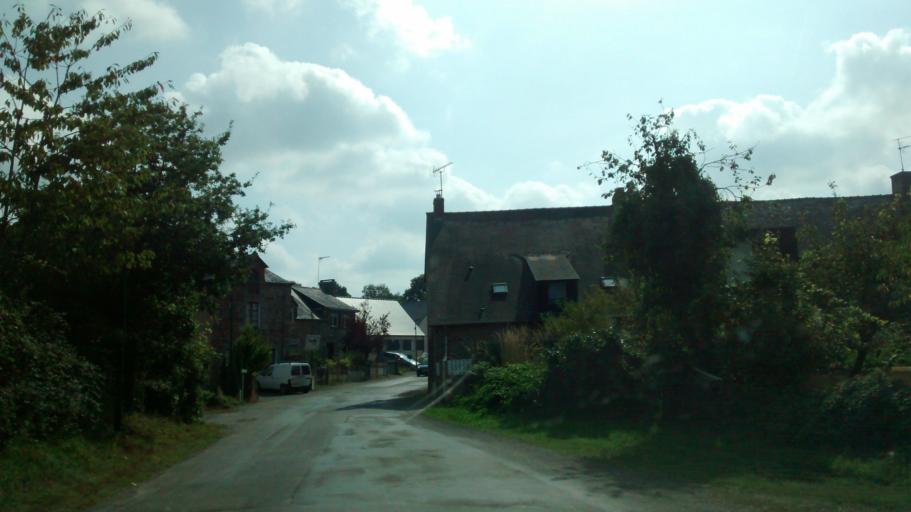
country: FR
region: Brittany
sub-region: Departement d'Ille-et-Vilaine
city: Livre-sur-Changeon
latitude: 48.2353
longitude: -1.3015
